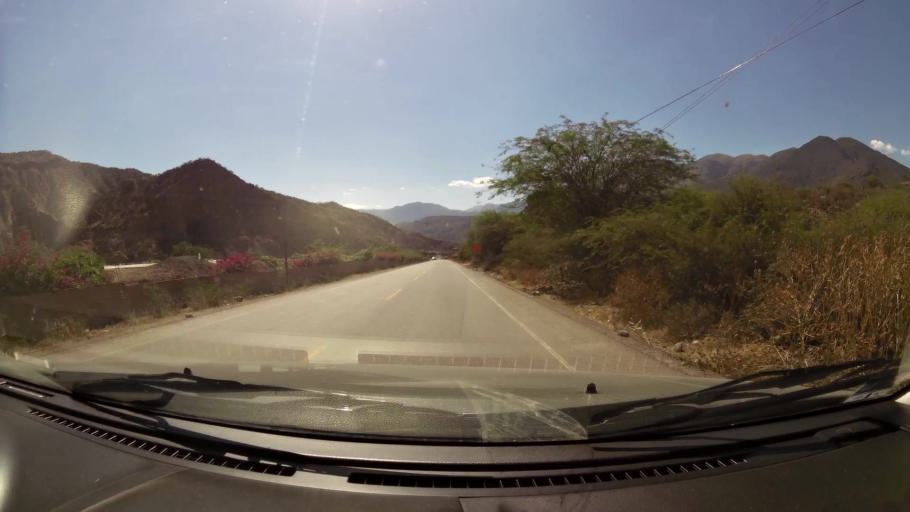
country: PE
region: Huancavelica
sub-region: Provincia de Acobamba
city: Marcas
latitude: -12.8524
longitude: -74.3309
